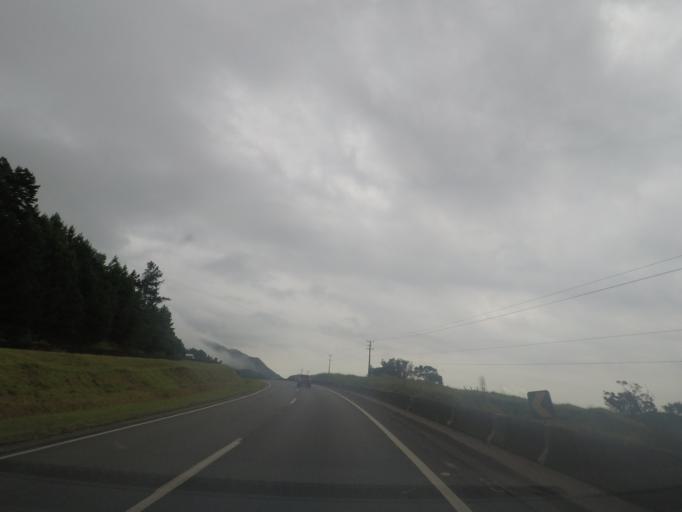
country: BR
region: Parana
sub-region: Campina Grande Do Sul
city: Campina Grande do Sul
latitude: -25.1539
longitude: -48.8613
